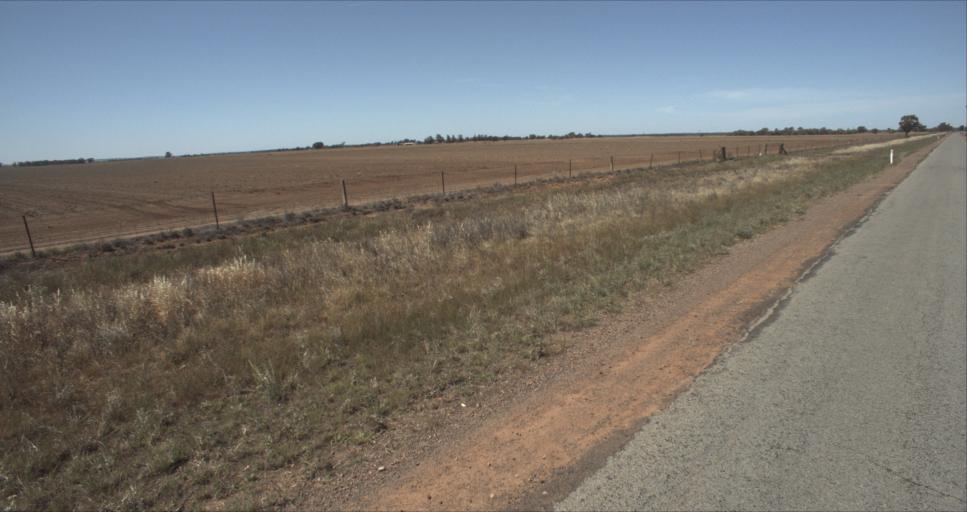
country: AU
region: New South Wales
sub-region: Leeton
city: Leeton
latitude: -34.5600
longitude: 146.3129
